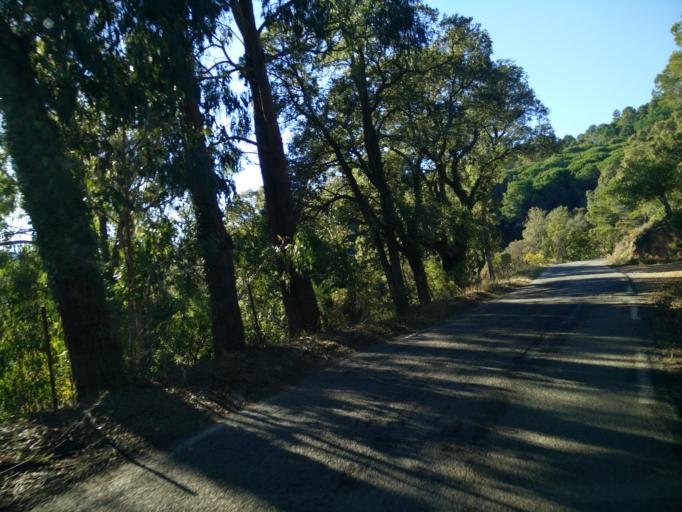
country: FR
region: Provence-Alpes-Cote d'Azur
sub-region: Departement du Var
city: La Garde-Freinet
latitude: 43.2569
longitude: 6.4101
